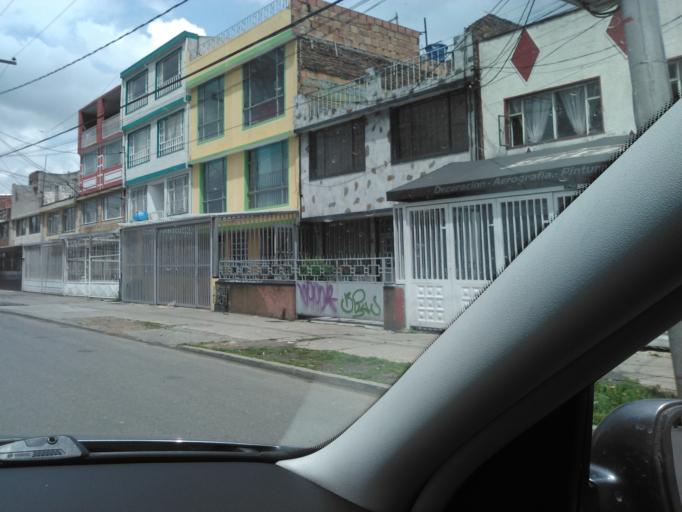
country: CO
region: Bogota D.C.
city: Bogota
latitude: 4.6183
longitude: -74.1068
